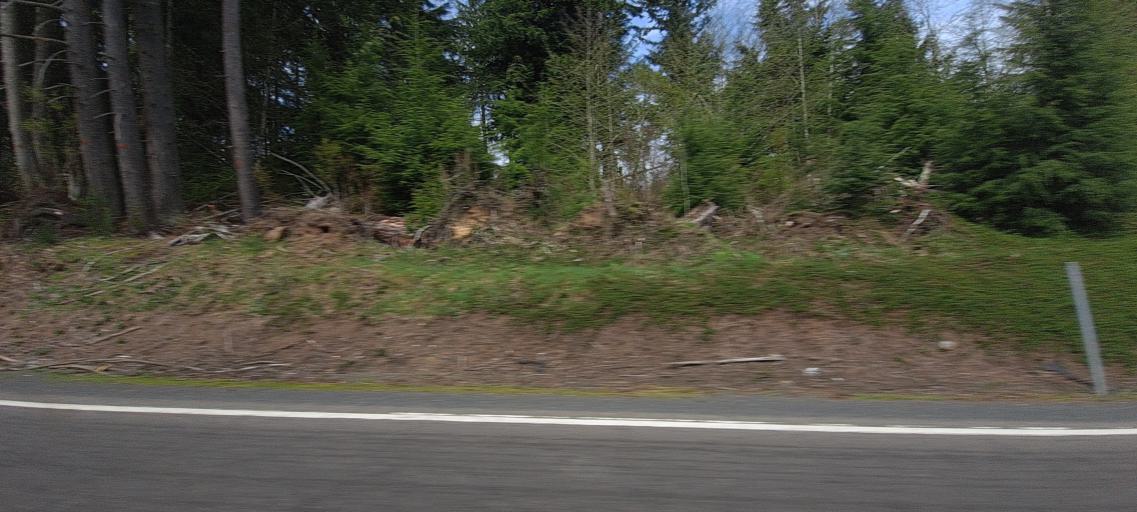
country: US
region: Oregon
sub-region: Clatsop County
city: Seaside
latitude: 45.9024
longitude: -123.6624
